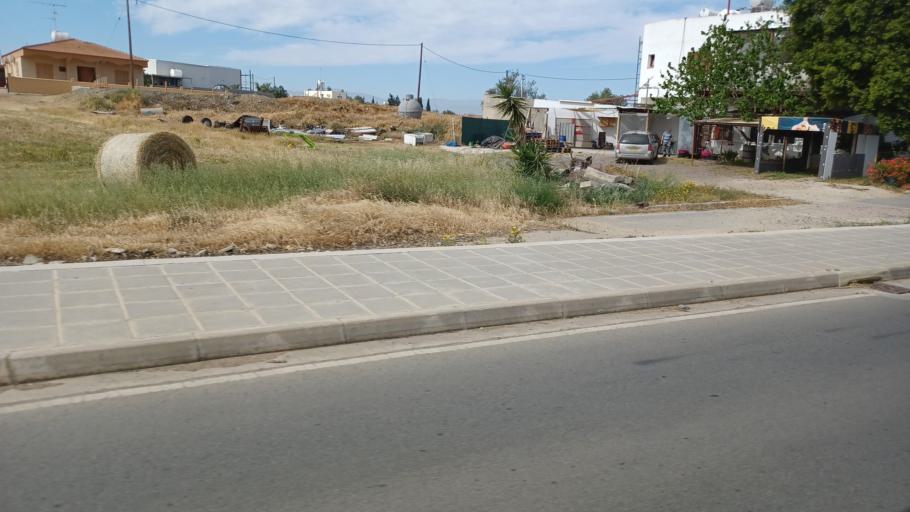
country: CY
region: Lefkosia
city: Kokkinotrimithia
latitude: 35.1541
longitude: 33.1952
